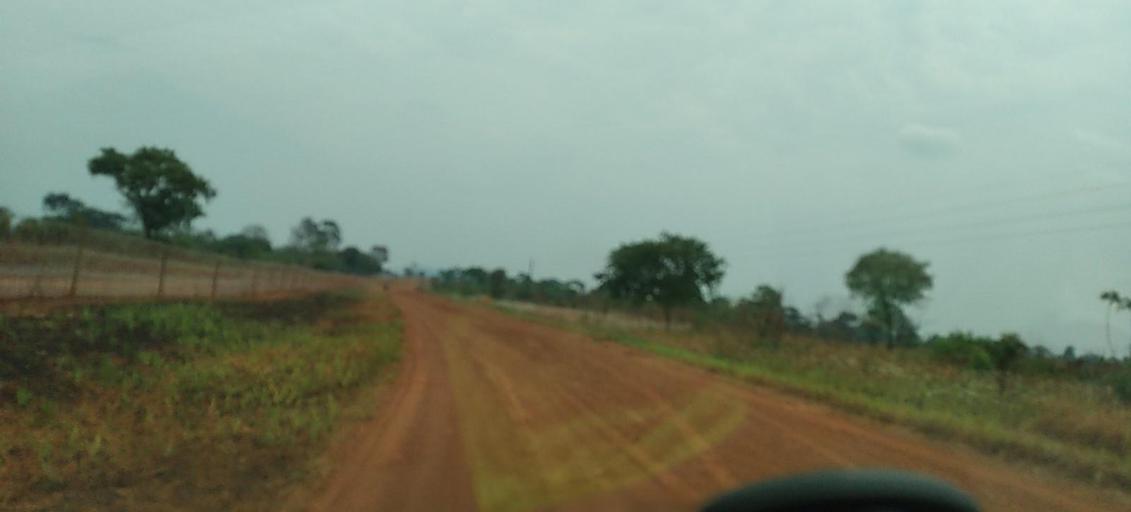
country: ZM
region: North-Western
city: Kansanshi
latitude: -12.0852
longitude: 26.4829
